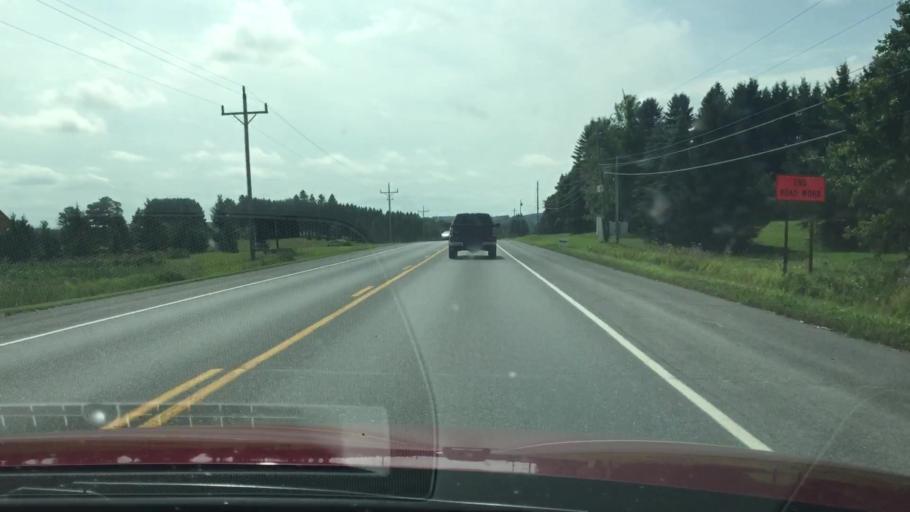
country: US
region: Maine
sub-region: Aroostook County
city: Easton
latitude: 46.4914
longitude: -67.8684
